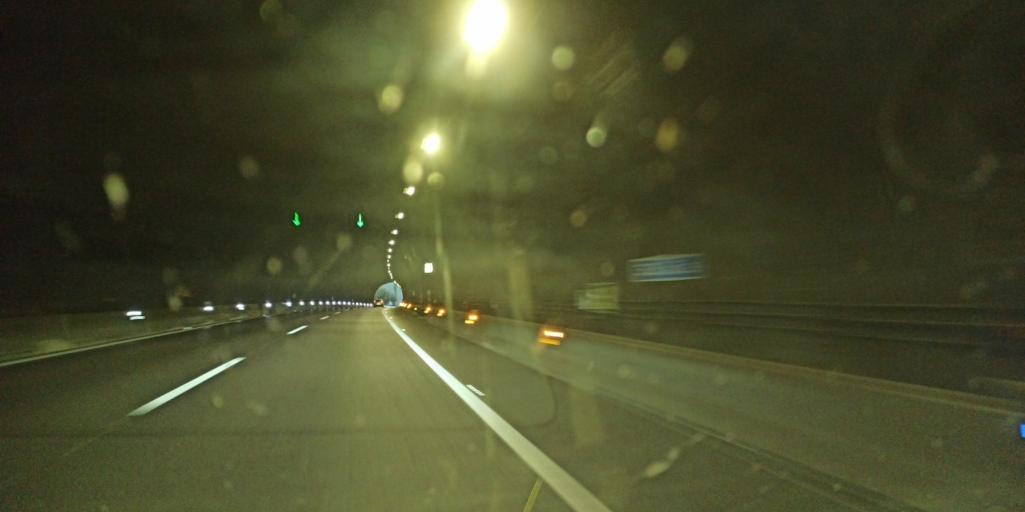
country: ES
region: Catalonia
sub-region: Provincia de Barcelona
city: Sitges
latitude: 41.2453
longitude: 1.8329
